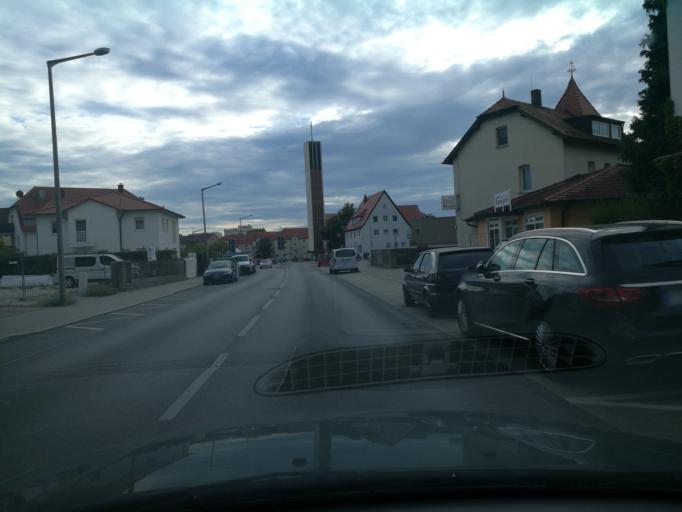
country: DE
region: Bavaria
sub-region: Regierungsbezirk Mittelfranken
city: Furth
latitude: 49.4838
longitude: 10.9709
